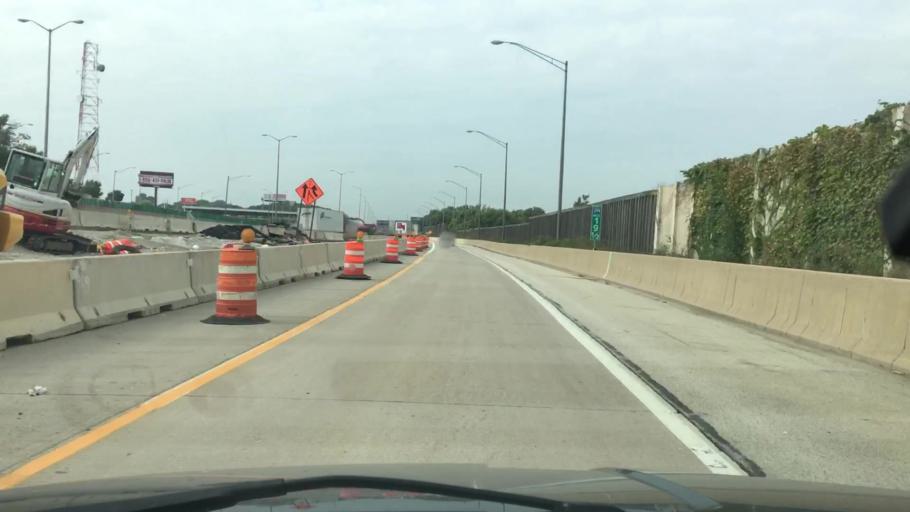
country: US
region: Illinois
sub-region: Cook County
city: Justice
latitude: 41.7411
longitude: -87.8288
